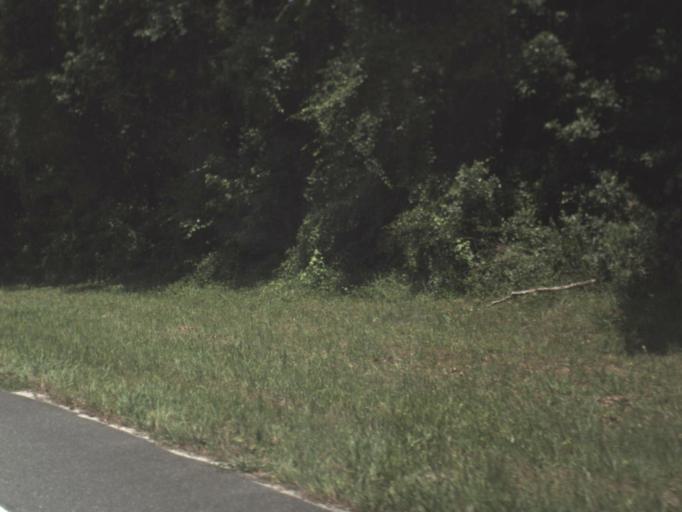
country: US
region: Florida
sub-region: Levy County
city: Williston
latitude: 29.4805
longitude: -82.4148
